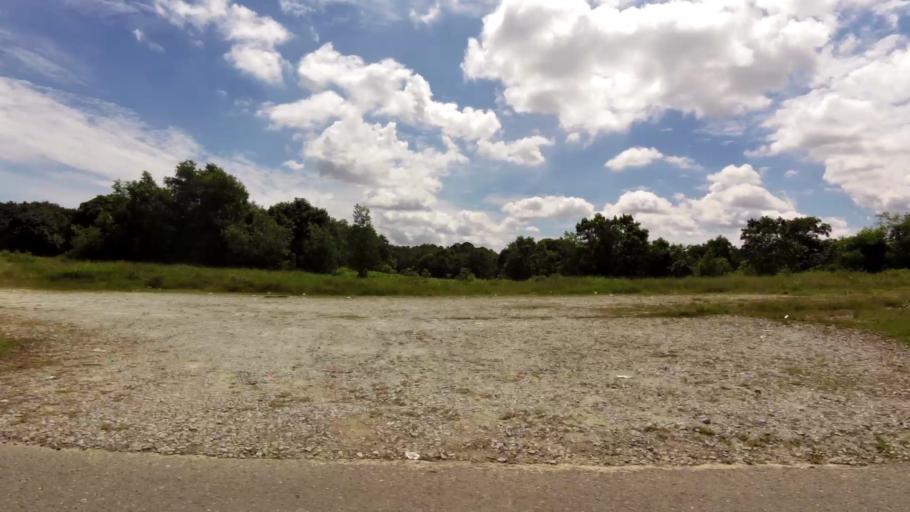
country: BN
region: Brunei and Muara
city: Bandar Seri Begawan
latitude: 4.9348
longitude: 114.8837
